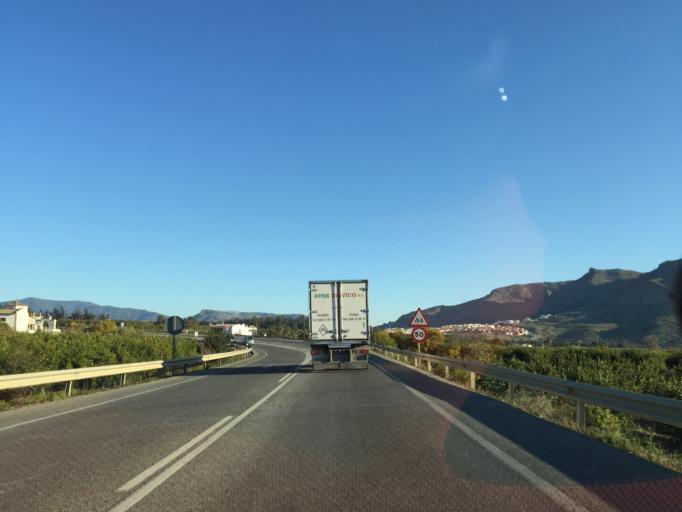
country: ES
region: Andalusia
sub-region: Provincia de Malaga
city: Pizarra
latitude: 36.7453
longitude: -4.7112
